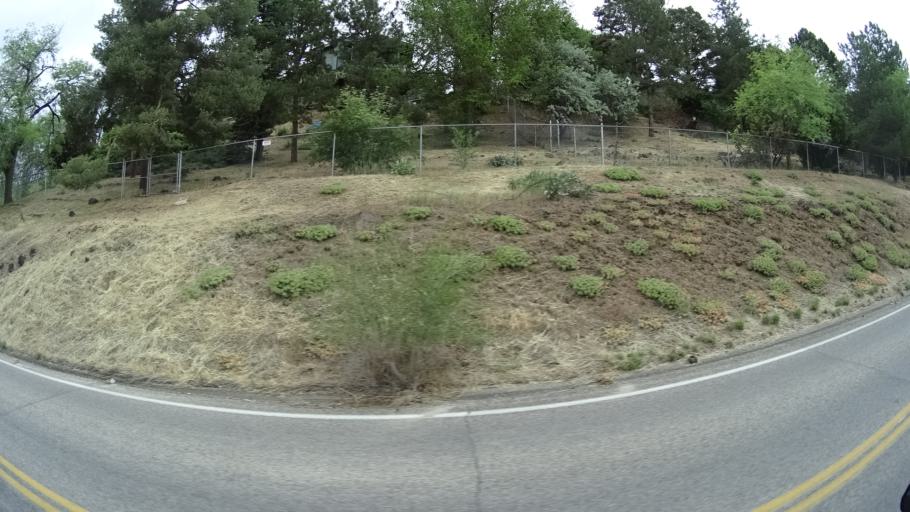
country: US
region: Idaho
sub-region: Ada County
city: Boise
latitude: 43.6141
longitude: -116.1810
